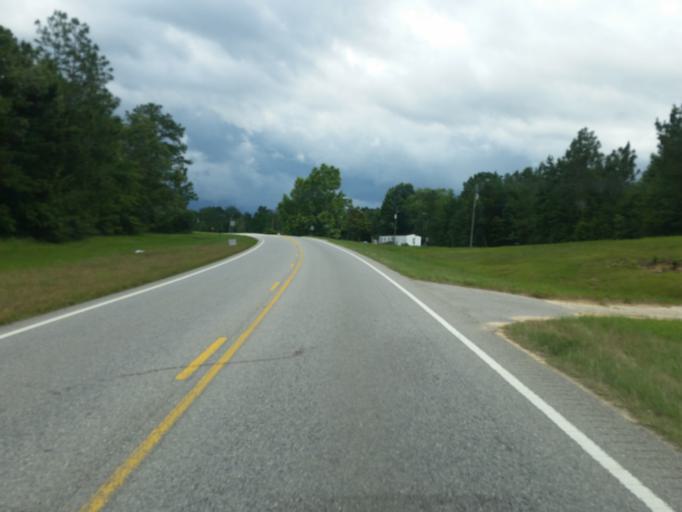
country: US
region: Mississippi
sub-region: George County
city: Lucedale
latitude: 30.8525
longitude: -88.4055
